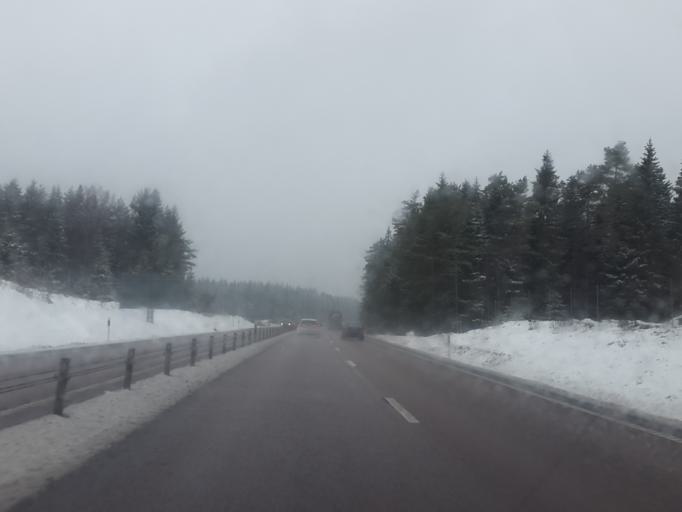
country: SE
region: Vaestra Goetaland
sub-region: Ulricehamns Kommun
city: Ulricehamn
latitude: 57.7799
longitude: 13.6589
